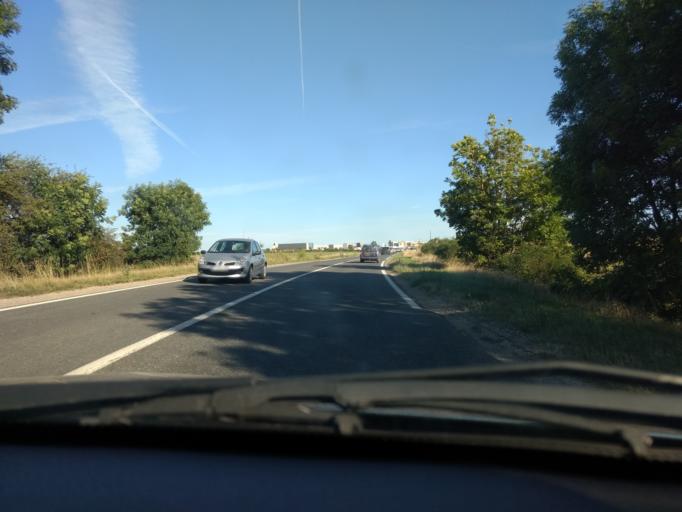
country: FR
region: Midi-Pyrenees
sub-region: Departement de l'Aveyron
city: Druelle
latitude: 44.3816
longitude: 2.5321
